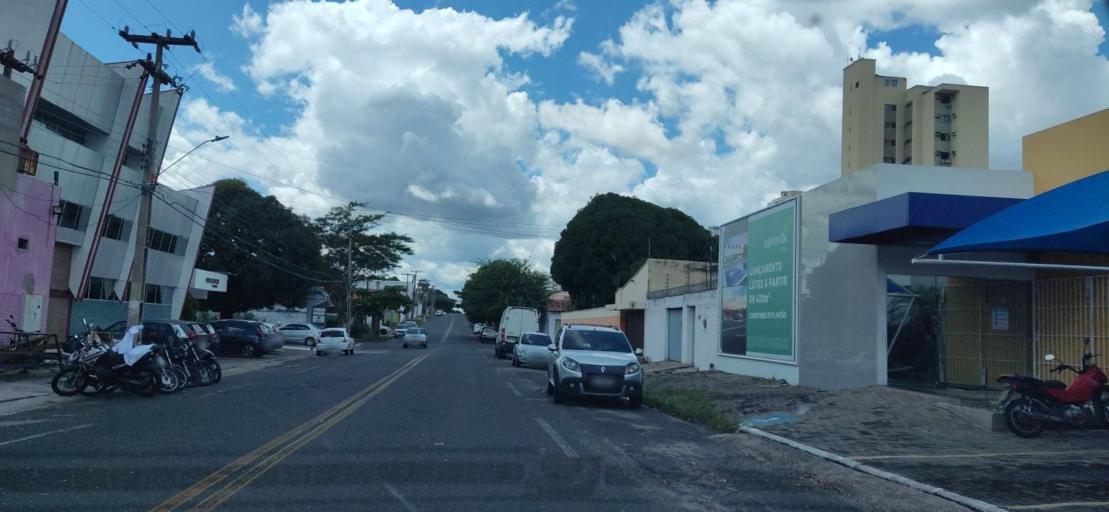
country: BR
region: Piaui
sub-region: Teresina
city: Teresina
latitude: -5.0726
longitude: -42.7908
